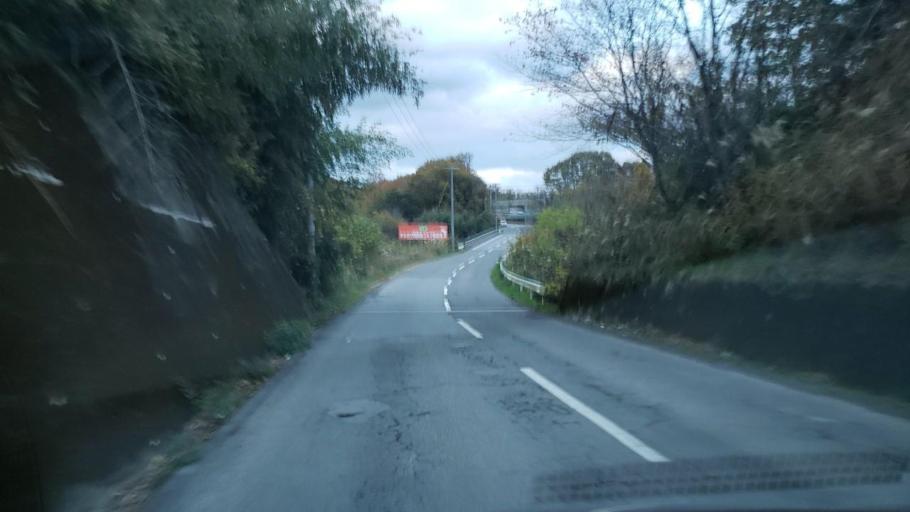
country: JP
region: Tokushima
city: Wakimachi
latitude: 34.0848
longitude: 134.1929
